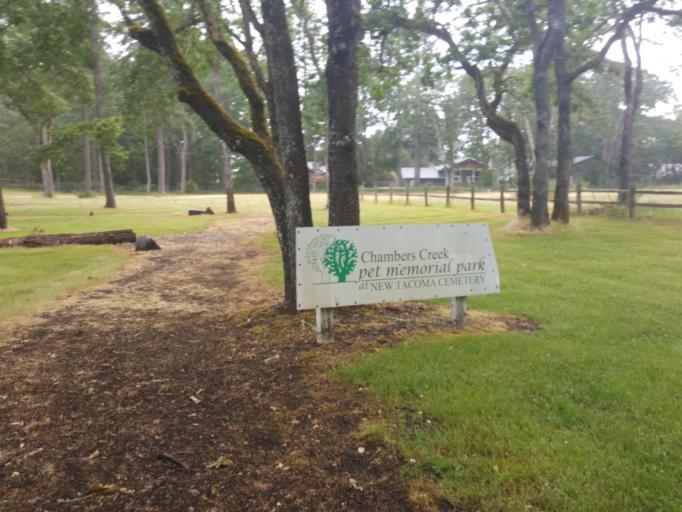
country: US
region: Washington
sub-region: Pierce County
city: University Place
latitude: 47.1999
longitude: -122.5646
